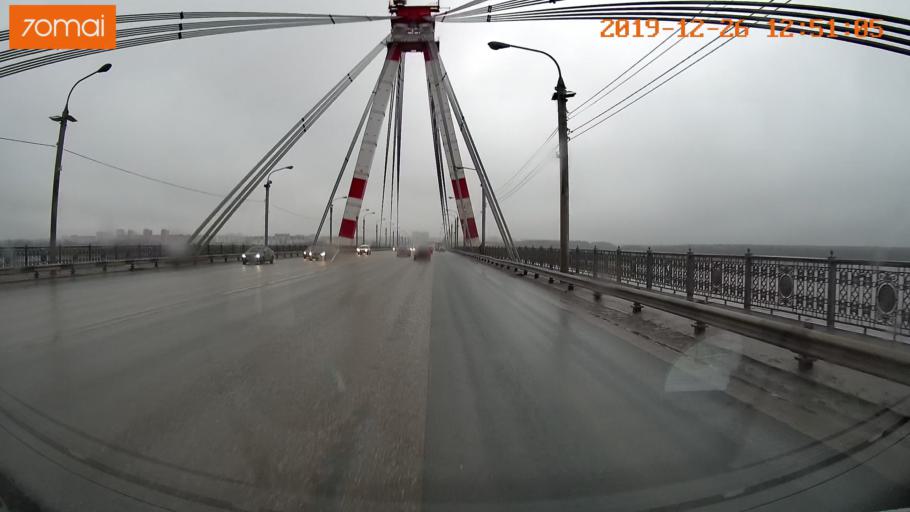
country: RU
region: Vologda
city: Cherepovets
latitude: 59.1148
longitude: 37.9029
